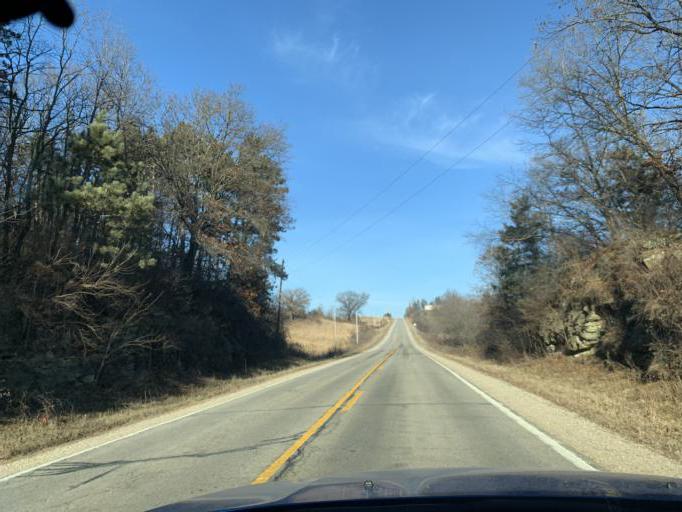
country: US
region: Wisconsin
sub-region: Green County
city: New Glarus
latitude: 42.7417
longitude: -89.8598
